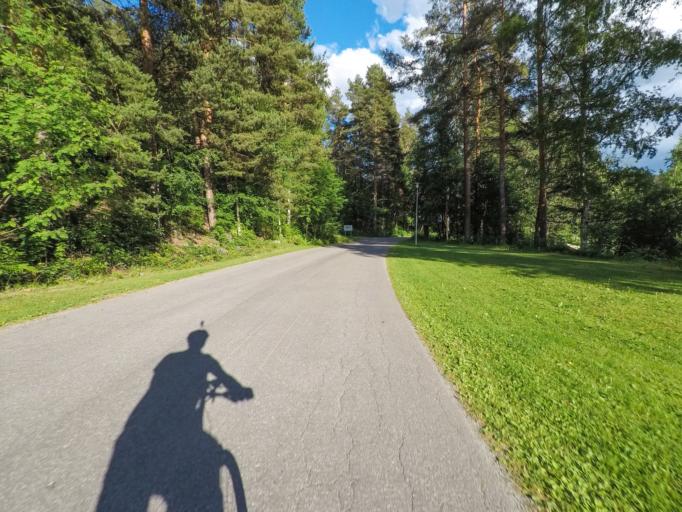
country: FI
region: Southern Savonia
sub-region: Savonlinna
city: Savonlinna
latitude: 61.8703
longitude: 28.8552
